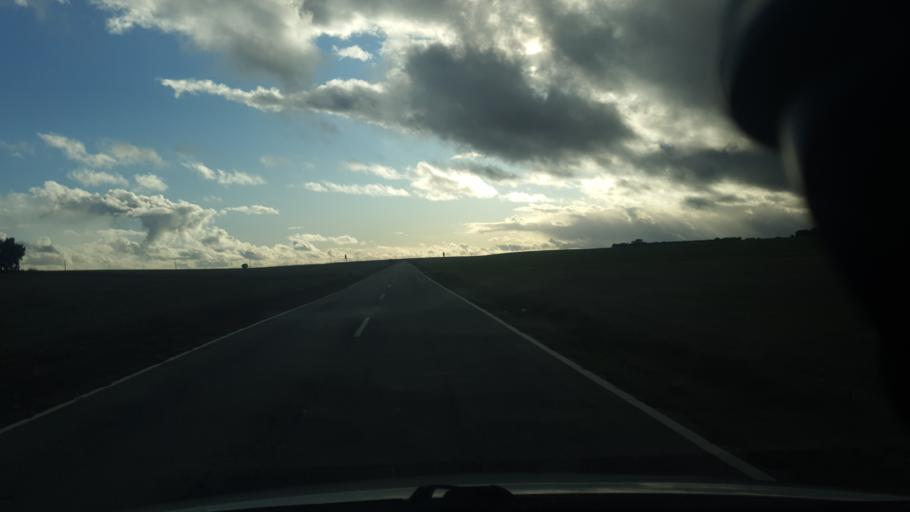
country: ES
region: Castille and Leon
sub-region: Provincia de Segovia
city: Santiuste de San Juan Bautista
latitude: 41.1359
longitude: -4.5954
